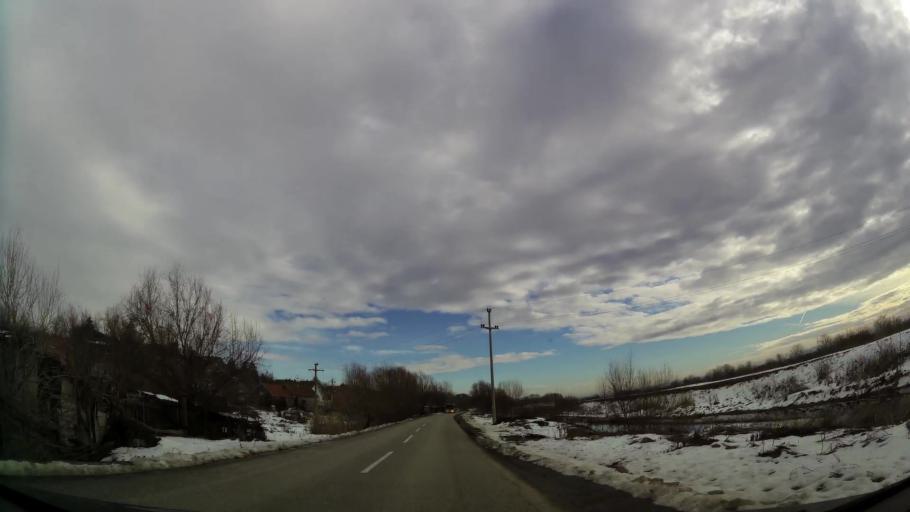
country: RS
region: Central Serbia
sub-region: Belgrade
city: Surcin
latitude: 44.7886
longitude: 20.2742
